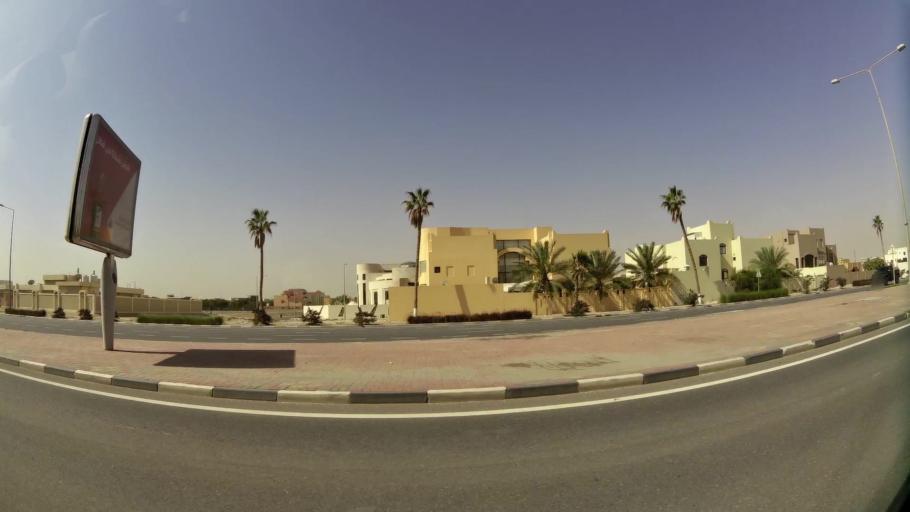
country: QA
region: Baladiyat ad Dawhah
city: Doha
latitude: 25.3518
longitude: 51.4996
